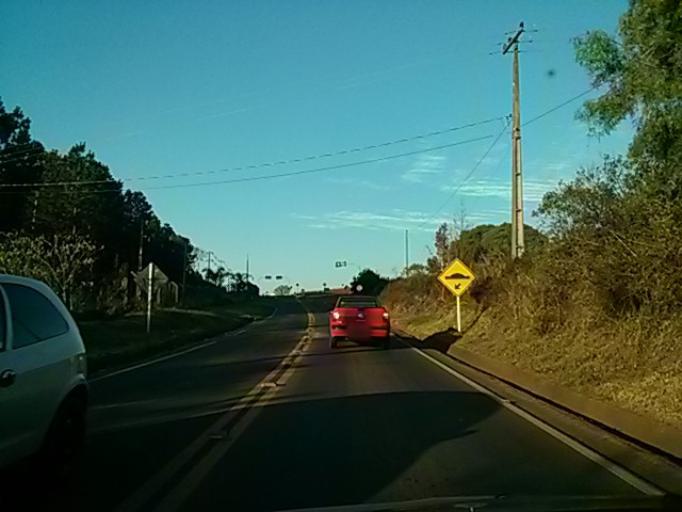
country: BR
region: Santa Catarina
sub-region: Chapeco
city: Chapeco
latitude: -27.1041
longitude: -52.7050
